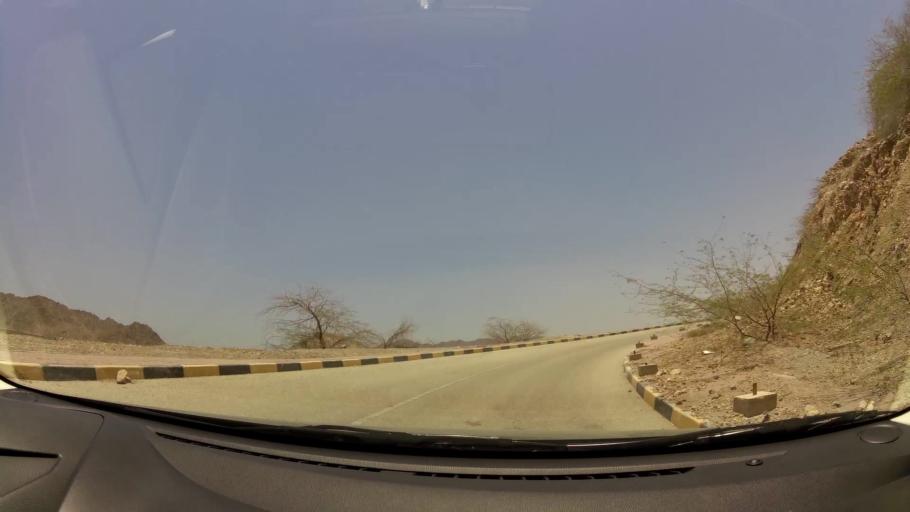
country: OM
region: Muhafazat Masqat
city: Muscat
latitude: 23.6177
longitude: 58.5359
